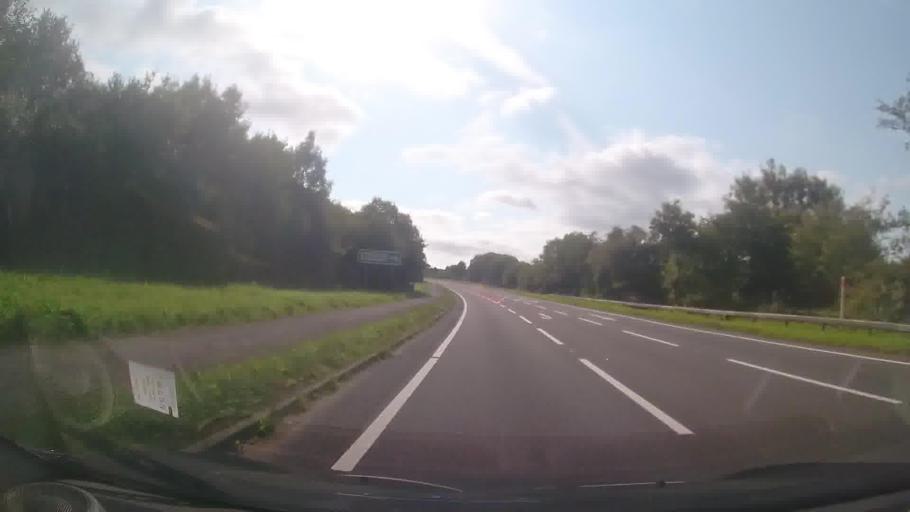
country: GB
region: Wales
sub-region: Pembrokeshire
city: Jeffreyston
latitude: 51.7068
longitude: -4.7683
